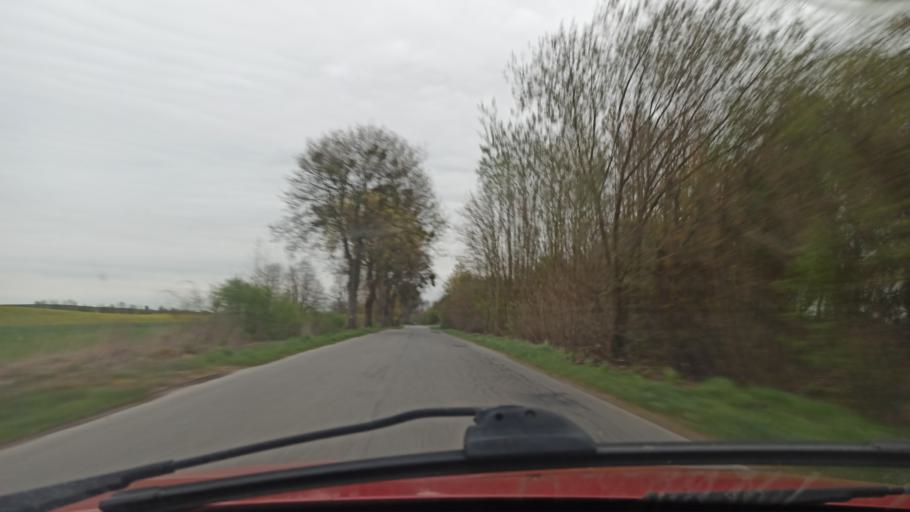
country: PL
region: Pomeranian Voivodeship
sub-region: Powiat kwidzynski
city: Gardeja
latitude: 53.5730
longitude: 18.9792
